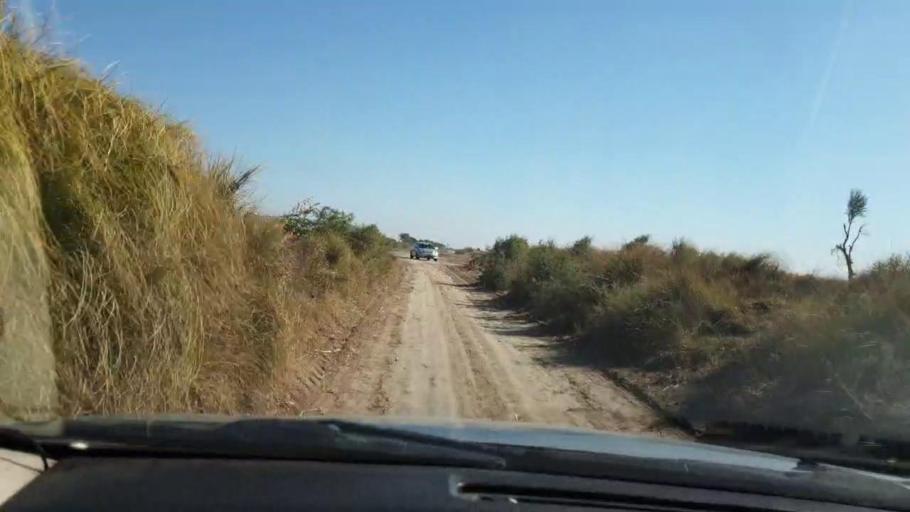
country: PK
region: Sindh
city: Berani
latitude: 25.7173
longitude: 68.9858
